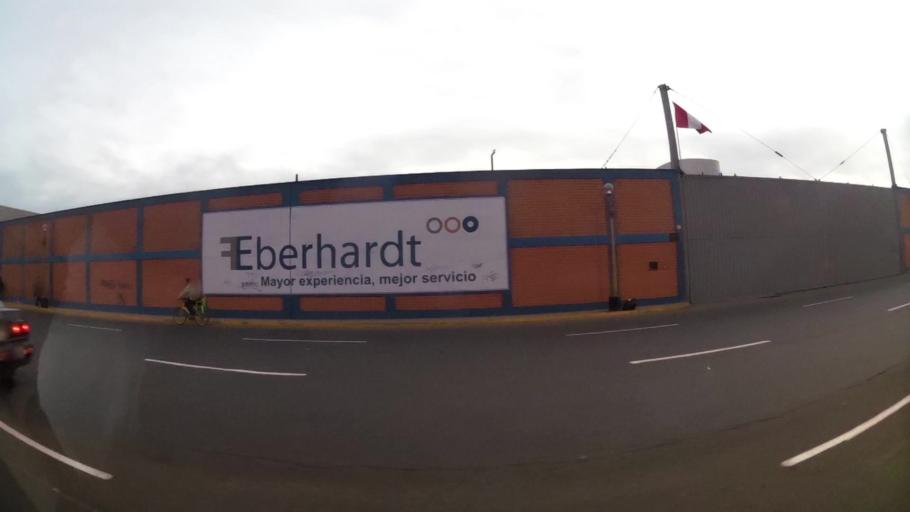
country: PE
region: Callao
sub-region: Callao
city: Callao
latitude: -12.0467
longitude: -77.0986
